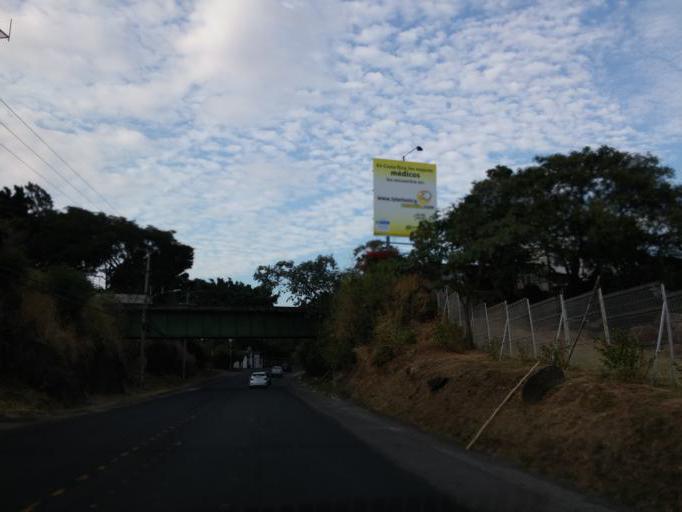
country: CR
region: Heredia
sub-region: Canton de Belen
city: San Antonio
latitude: 9.9755
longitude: -84.1998
